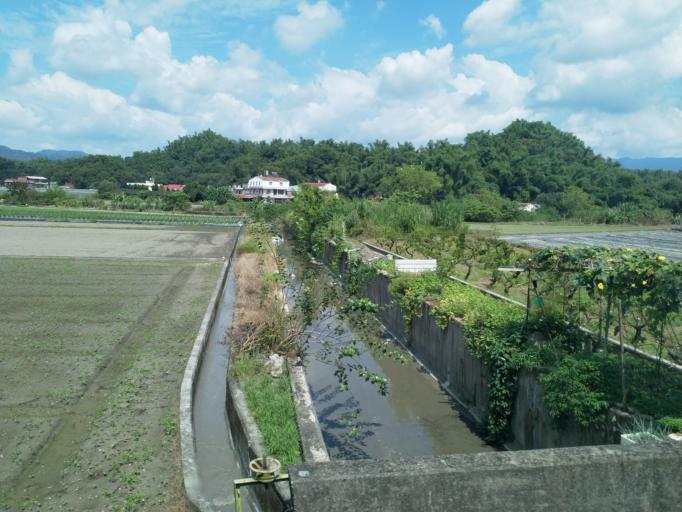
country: TW
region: Taiwan
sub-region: Pingtung
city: Pingtung
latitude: 22.8810
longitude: 120.5605
